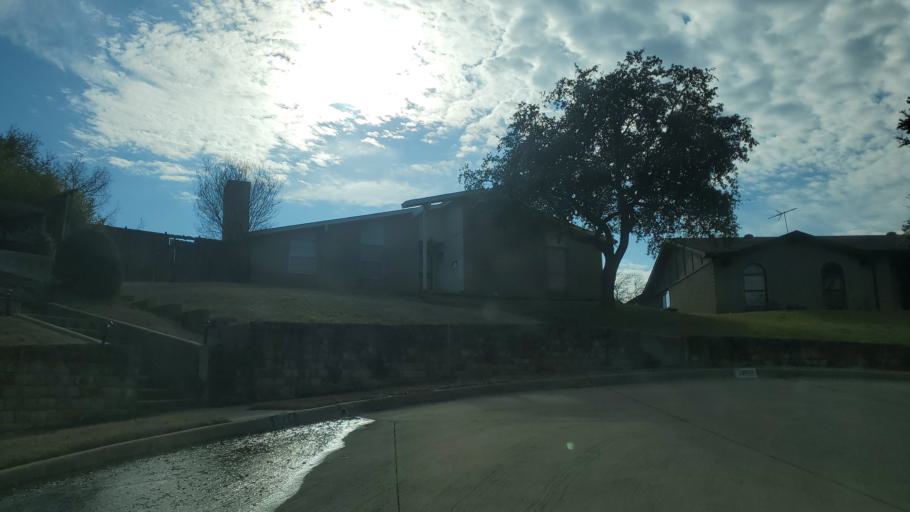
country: US
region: Texas
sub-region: Dallas County
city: Carrollton
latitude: 32.9947
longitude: -96.8910
